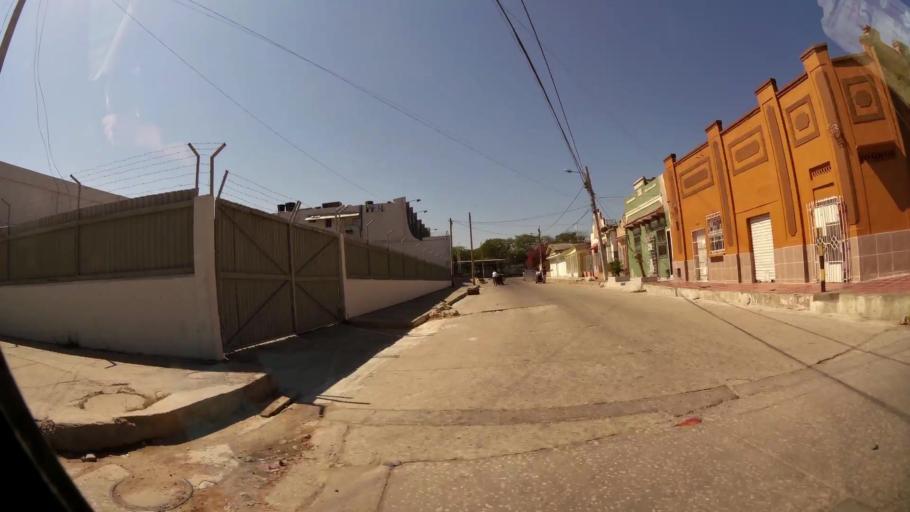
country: CO
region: Atlantico
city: Barranquilla
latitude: 10.9768
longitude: -74.7868
